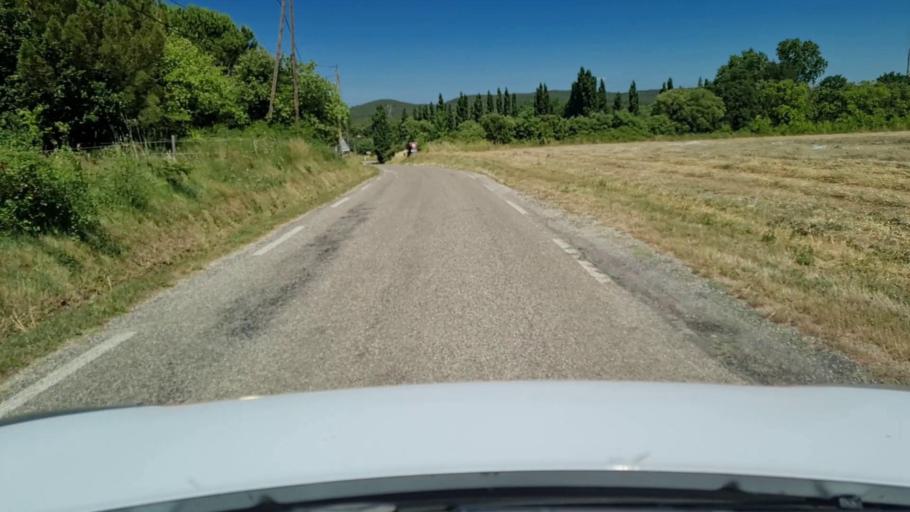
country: FR
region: Languedoc-Roussillon
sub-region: Departement du Gard
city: Saint-Mamert-du-Gard
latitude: 43.8553
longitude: 4.1584
